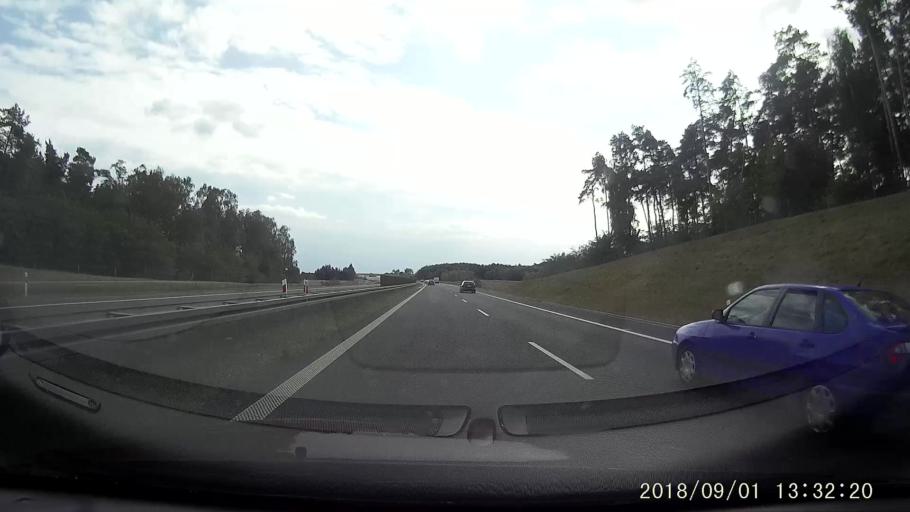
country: PL
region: West Pomeranian Voivodeship
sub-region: Powiat mysliborski
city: Mysliborz
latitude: 53.0001
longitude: 14.8619
